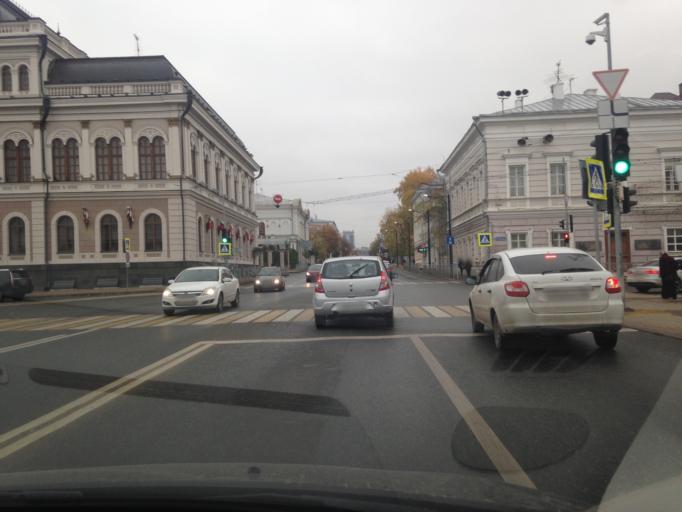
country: RU
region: Tatarstan
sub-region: Gorod Kazan'
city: Kazan
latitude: 55.7962
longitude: 49.1253
